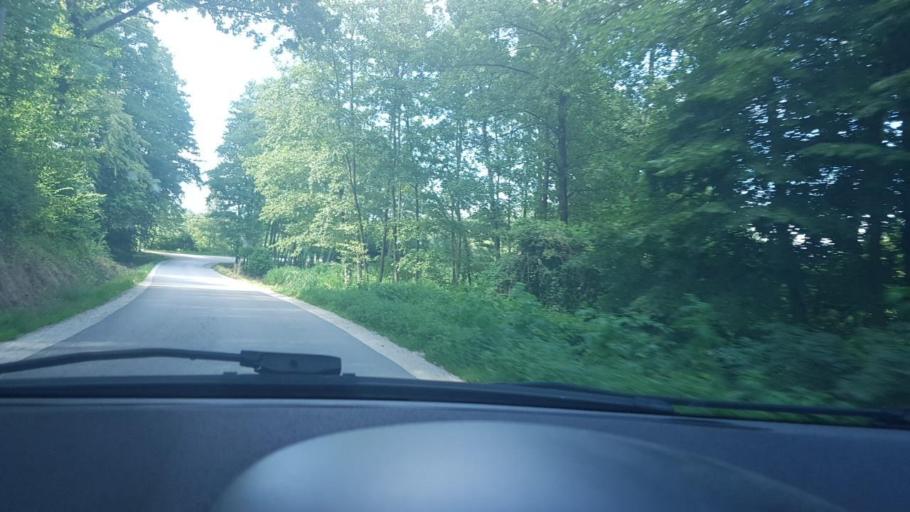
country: HR
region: Varazdinska
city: Tuzno
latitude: 46.2681
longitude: 16.1927
